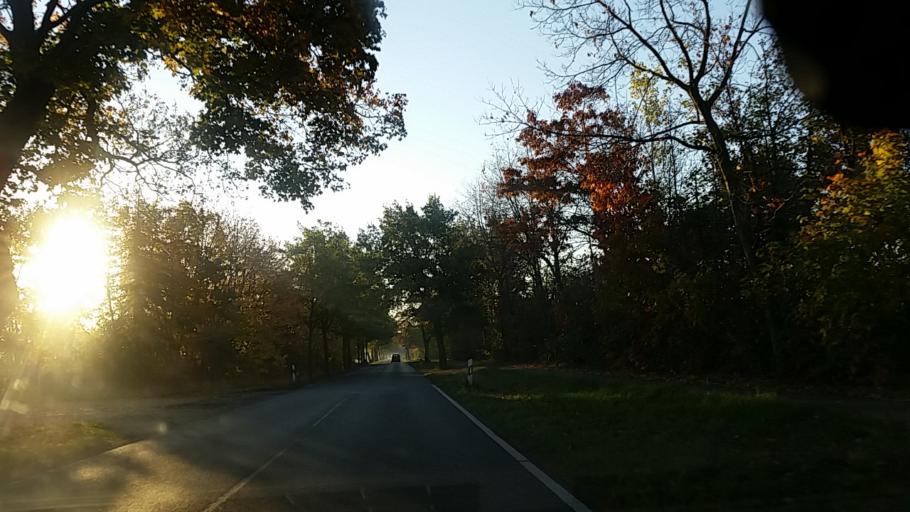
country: DE
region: Lower Saxony
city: Jembke
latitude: 52.4679
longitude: 10.7772
